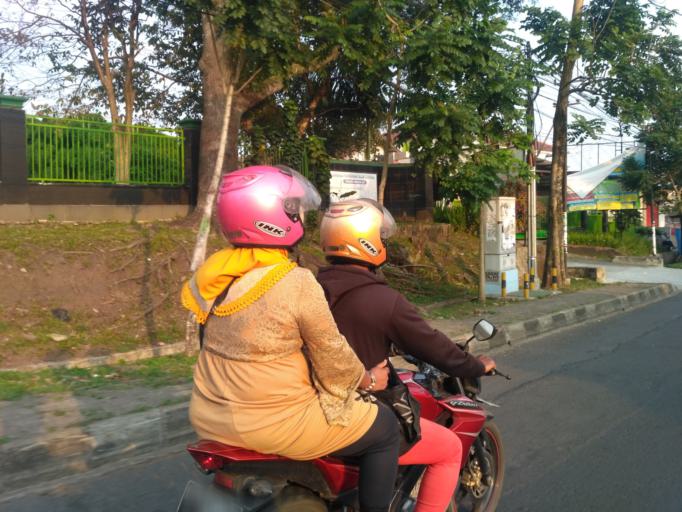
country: ID
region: East Java
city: Kepuh
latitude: -8.0016
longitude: 112.6178
